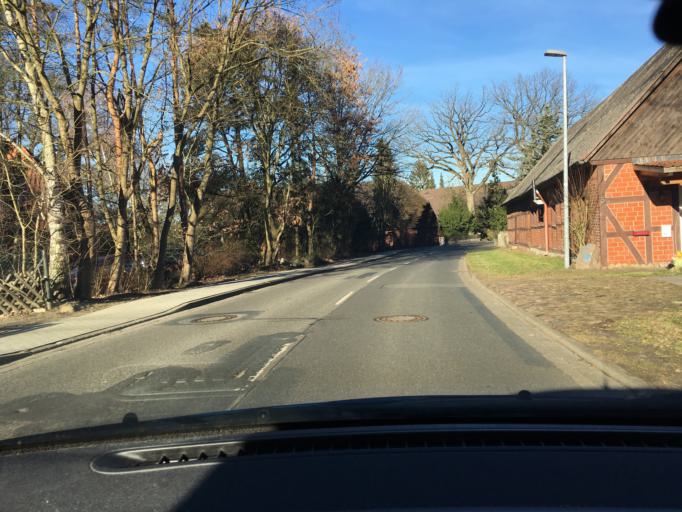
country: DE
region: Lower Saxony
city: Barnstedt
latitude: 53.1564
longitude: 10.3805
